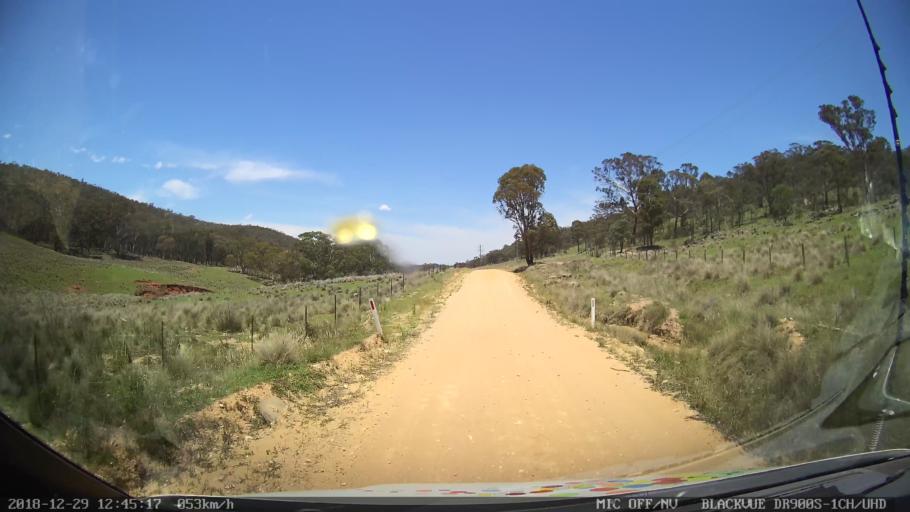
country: AU
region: Australian Capital Territory
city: Macarthur
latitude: -35.6339
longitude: 149.2149
